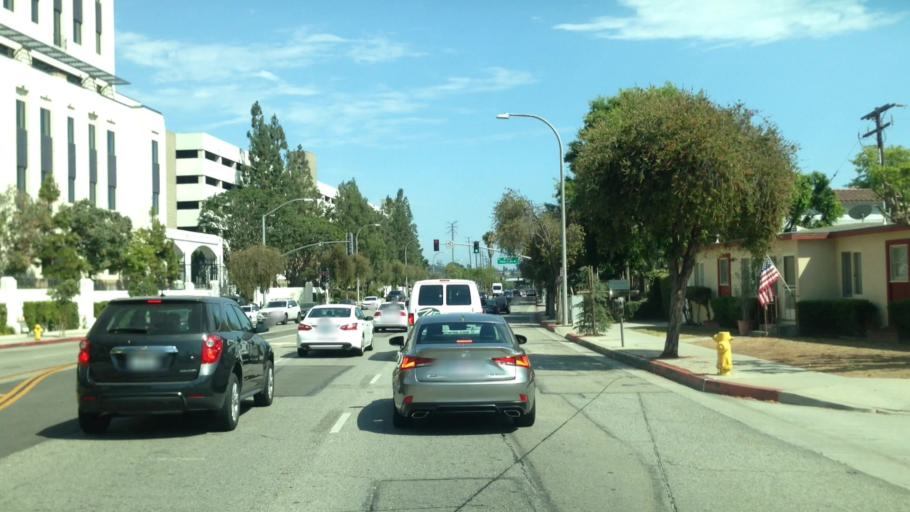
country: US
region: California
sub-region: Los Angeles County
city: Culver City
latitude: 34.0163
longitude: -118.4050
